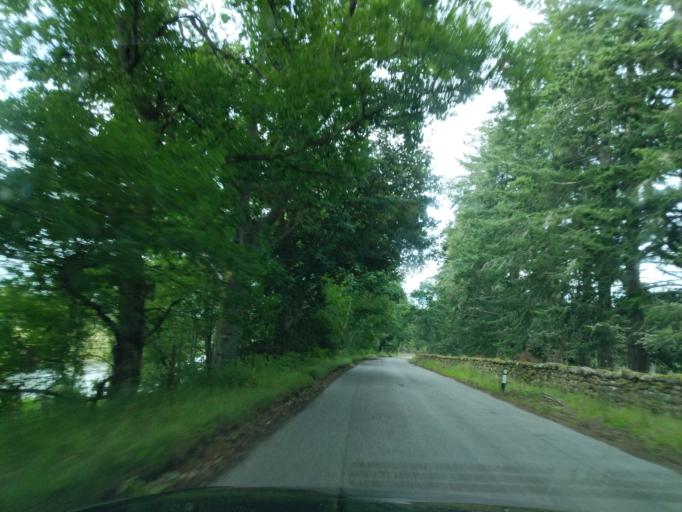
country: GB
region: Scotland
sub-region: Aberdeenshire
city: Aboyne
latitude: 57.0717
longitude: -2.8870
